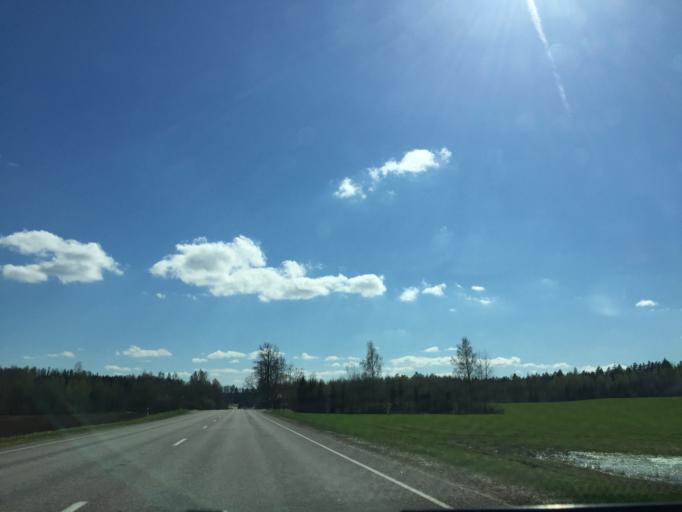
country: EE
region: Valgamaa
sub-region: Valga linn
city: Valga
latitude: 57.8726
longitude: 26.0600
